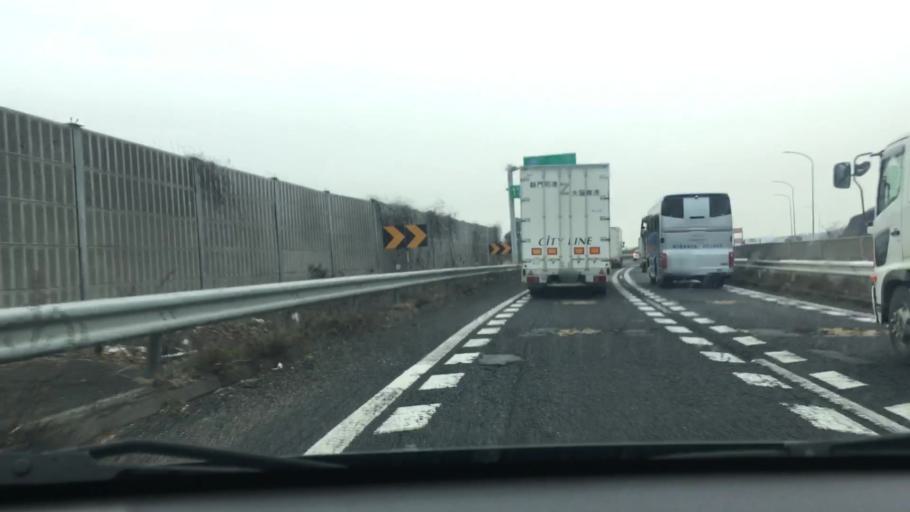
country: JP
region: Mie
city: Ueno-ebisumachi
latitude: 34.7894
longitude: 136.1610
